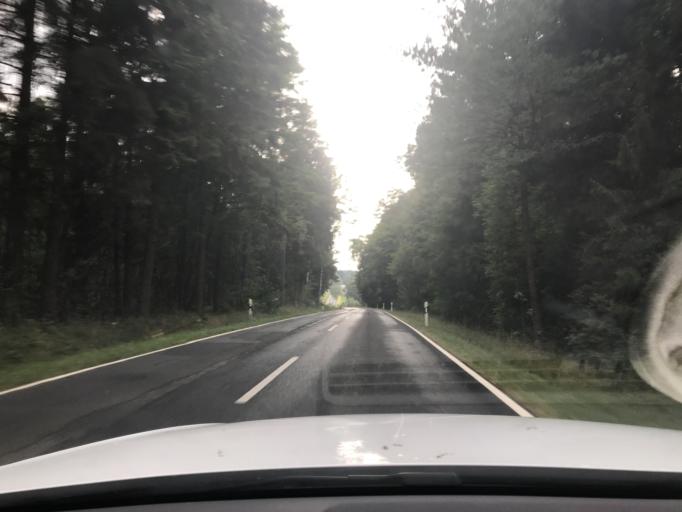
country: DE
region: Bavaria
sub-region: Upper Franconia
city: Prebitz
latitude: 49.7977
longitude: 11.6594
